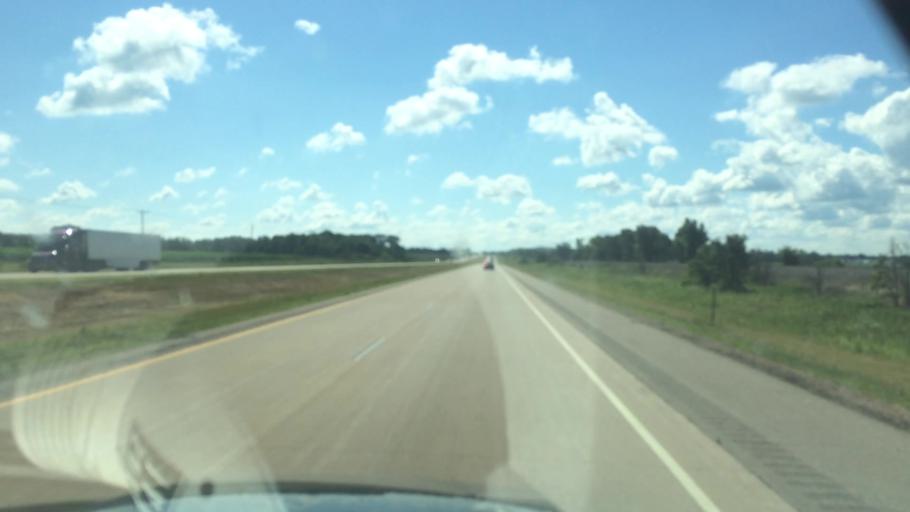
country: US
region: Wisconsin
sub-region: Portage County
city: Amherst
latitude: 44.4913
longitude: -89.3608
